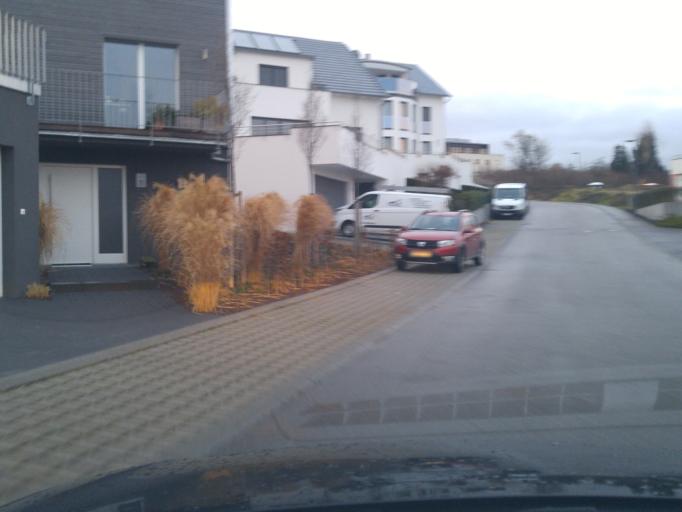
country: DE
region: Baden-Wuerttemberg
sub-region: Regierungsbezirk Stuttgart
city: Waiblingen
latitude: 48.8396
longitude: 9.3274
